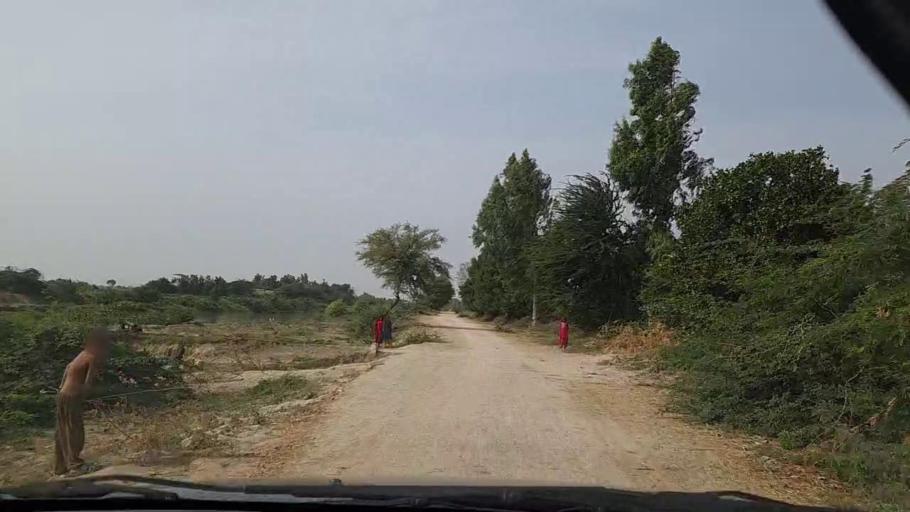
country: PK
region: Sindh
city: Thatta
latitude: 24.5691
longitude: 67.8601
